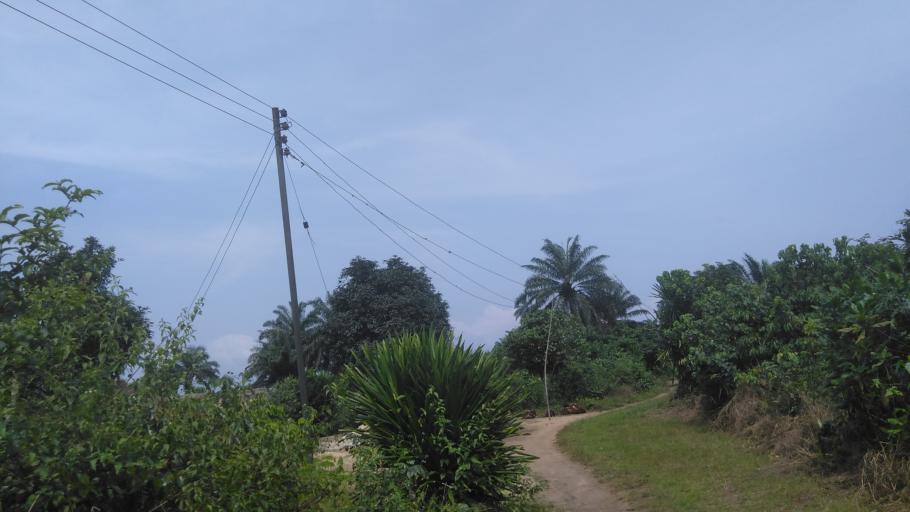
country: NG
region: Abia
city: Aba
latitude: 5.0464
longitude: 7.2499
